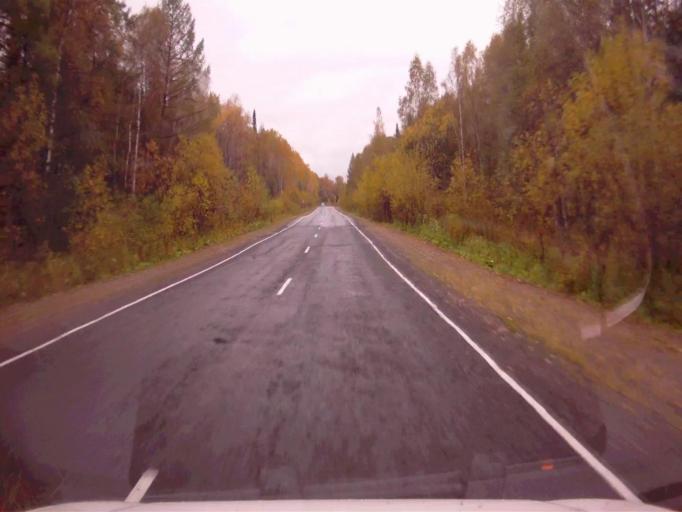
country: RU
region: Chelyabinsk
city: Nizhniy Ufaley
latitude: 56.0640
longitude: 59.9993
